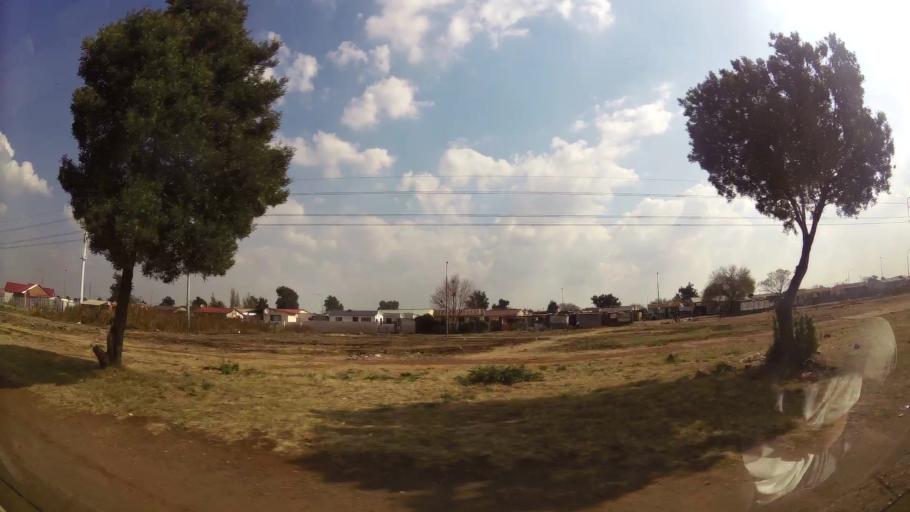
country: ZA
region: Gauteng
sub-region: Ekurhuleni Metropolitan Municipality
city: Germiston
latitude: -26.3356
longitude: 28.1439
